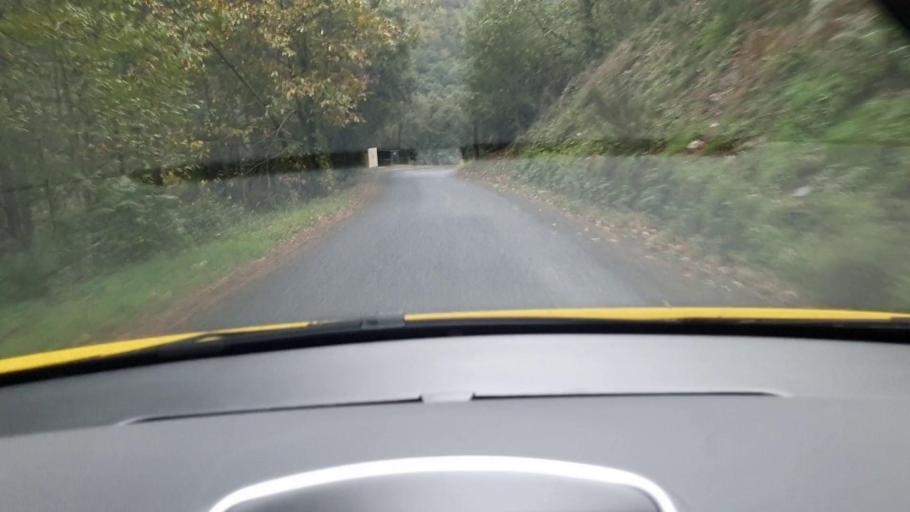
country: FR
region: Languedoc-Roussillon
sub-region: Departement du Gard
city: Sumene
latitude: 44.0296
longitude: 3.7368
